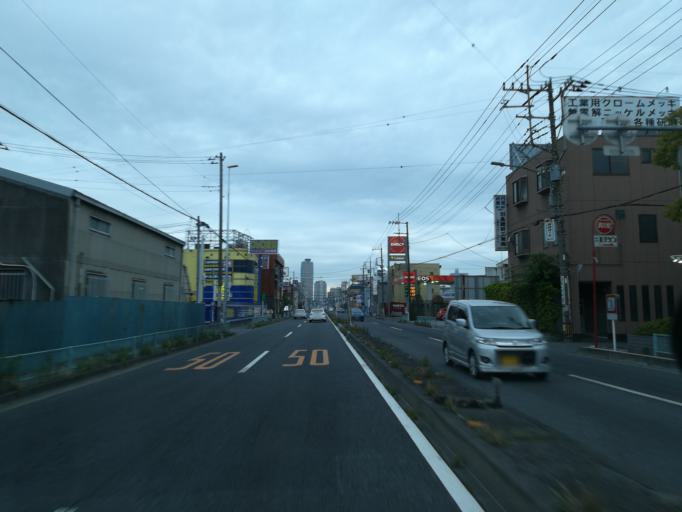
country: JP
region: Saitama
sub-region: Kawaguchi-shi
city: Hatogaya-honcho
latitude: 35.8147
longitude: 139.7357
